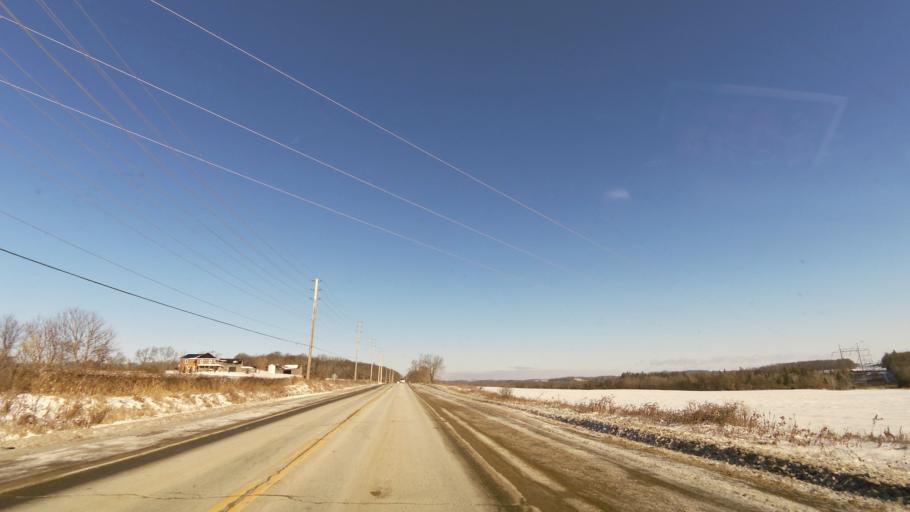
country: CA
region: Ontario
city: Quinte West
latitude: 44.2344
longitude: -77.8207
